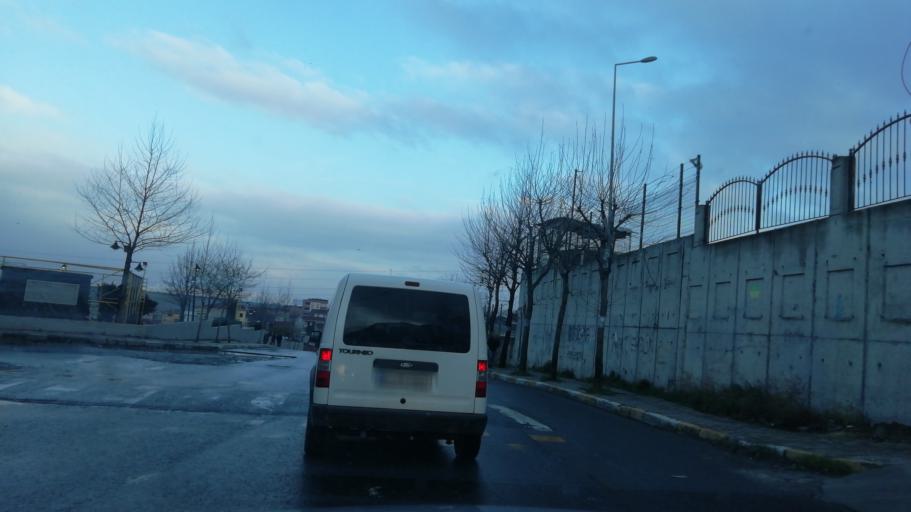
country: TR
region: Istanbul
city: Esenyurt
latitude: 41.0288
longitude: 28.7001
